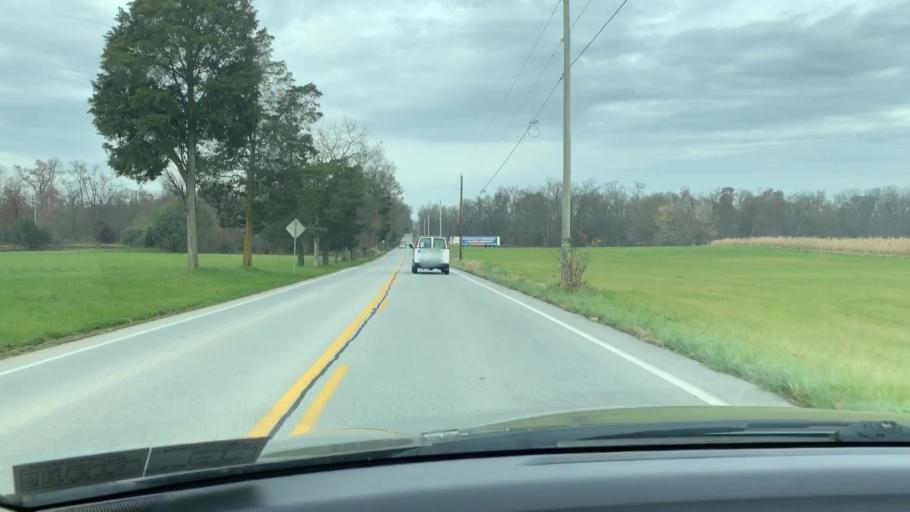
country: US
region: Pennsylvania
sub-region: Adams County
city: Lake Meade
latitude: 39.9411
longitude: -77.0696
